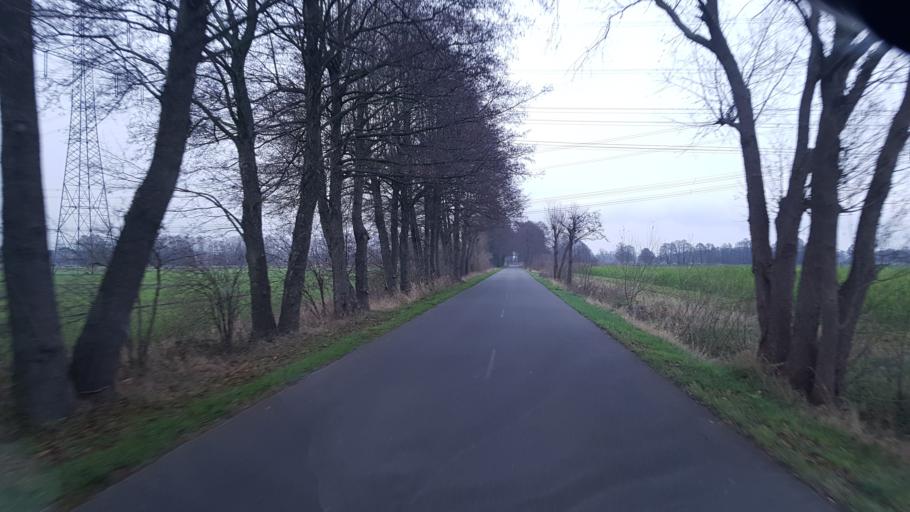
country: DE
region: Brandenburg
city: Peitz
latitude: 51.8847
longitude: 14.4045
